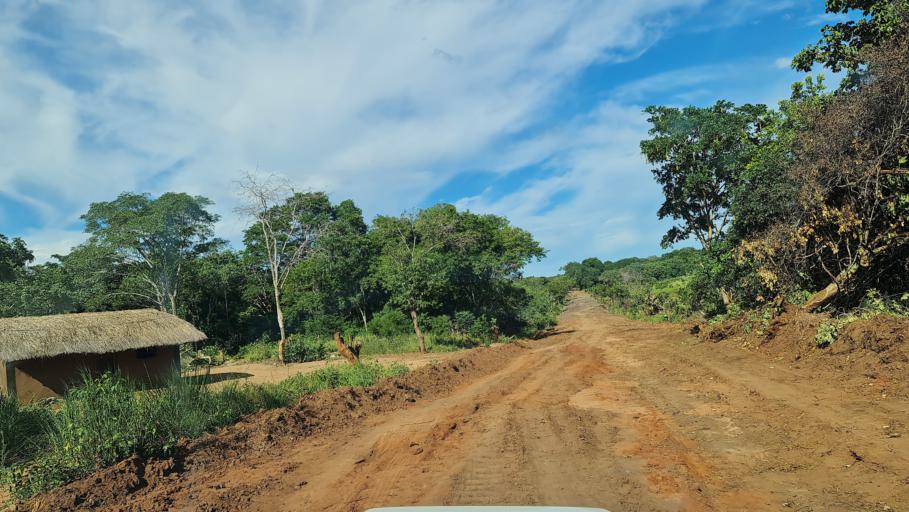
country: MZ
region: Nampula
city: Antonio Enes
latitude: -15.5084
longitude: 40.1397
